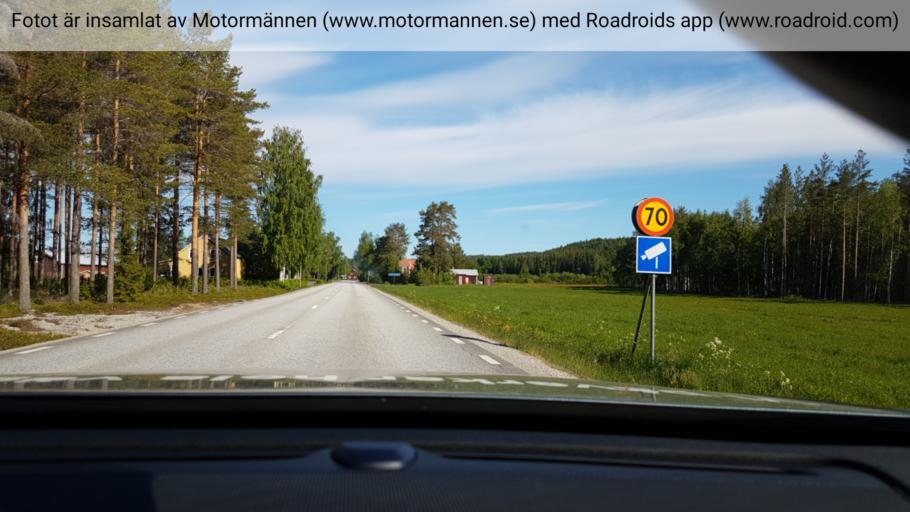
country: SE
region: Vaesterbotten
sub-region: Vindelns Kommun
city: Vindeln
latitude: 64.1177
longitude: 19.5663
